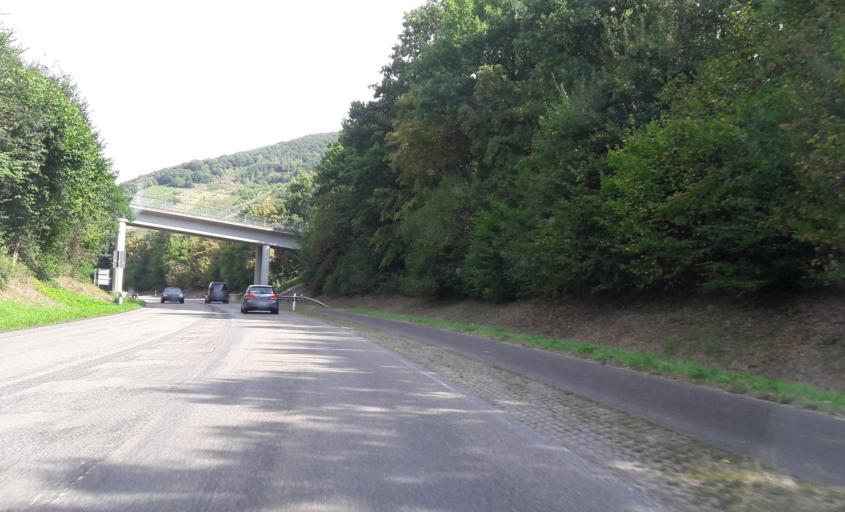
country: DE
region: Rheinland-Pfalz
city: Nehren
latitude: 50.0844
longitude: 7.2020
